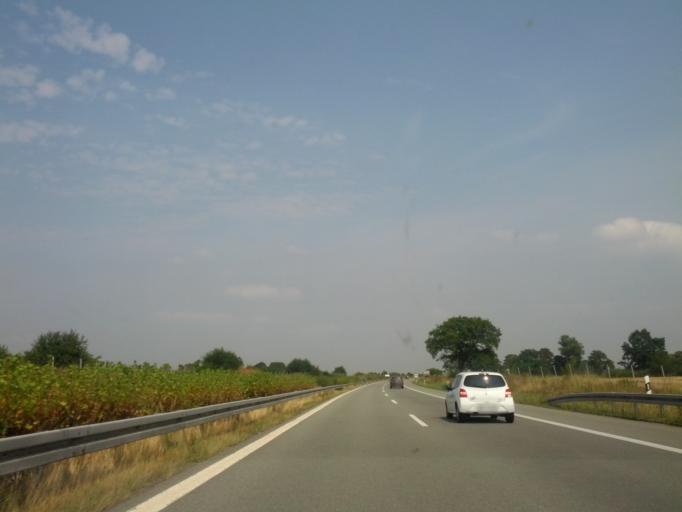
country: DE
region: Mecklenburg-Vorpommern
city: Bad Sulze
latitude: 54.0431
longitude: 12.6113
